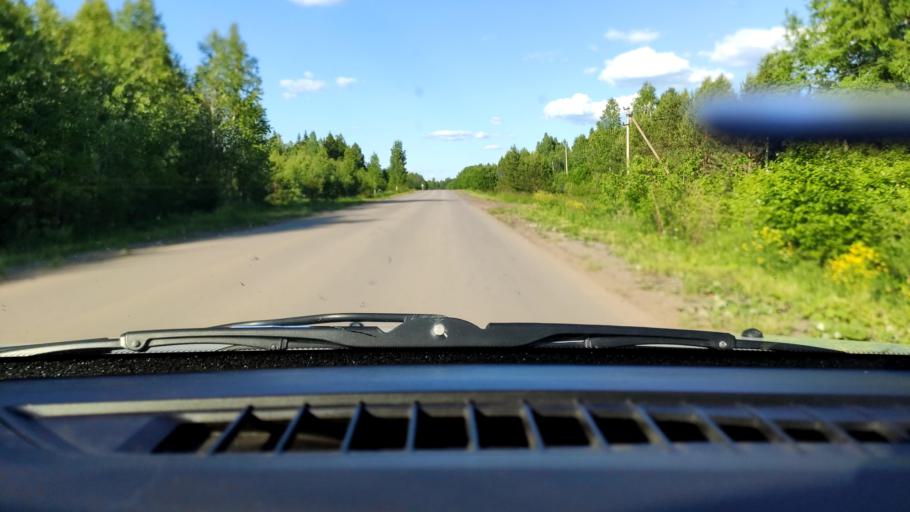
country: RU
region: Perm
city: Orda
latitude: 57.1297
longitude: 56.6964
